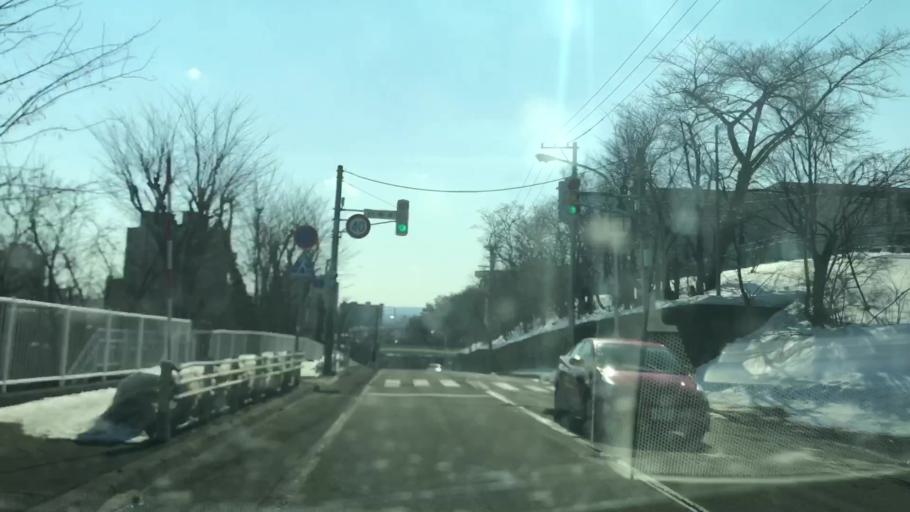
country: JP
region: Hokkaido
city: Sapporo
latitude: 43.0346
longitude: 141.3312
